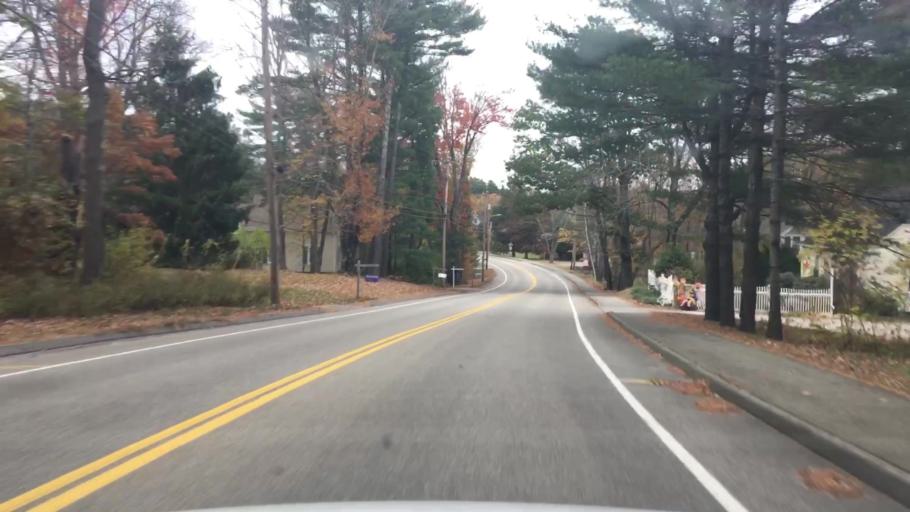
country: US
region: Maine
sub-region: Cumberland County
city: Falmouth
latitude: 43.7280
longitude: -70.2452
